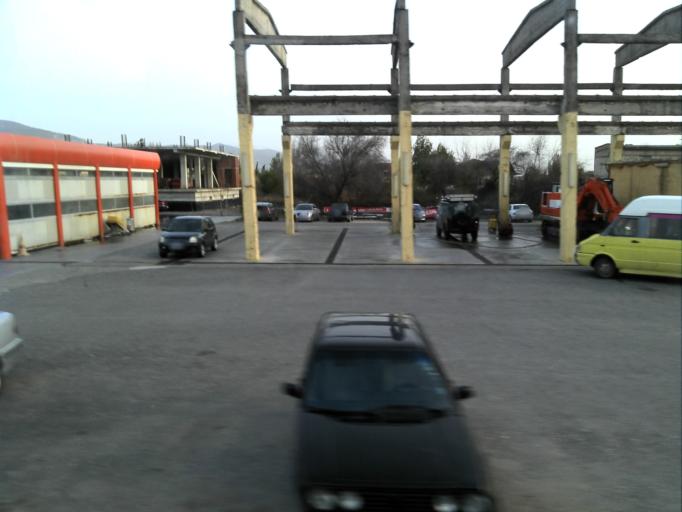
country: AL
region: Lezhe
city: Lezhe
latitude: 41.7781
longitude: 19.6365
